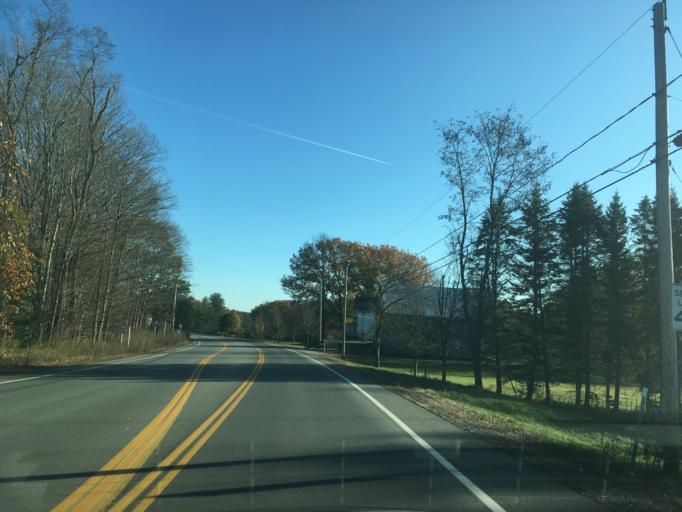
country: US
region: New Hampshire
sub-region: Rockingham County
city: Stratham Station
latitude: 43.0417
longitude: -70.9303
